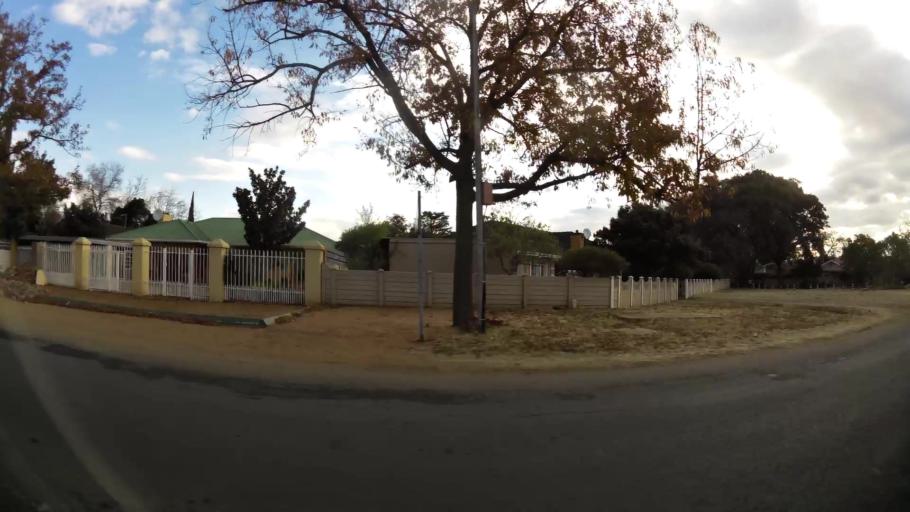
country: ZA
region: Orange Free State
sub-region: Lejweleputswa District Municipality
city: Welkom
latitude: -27.9964
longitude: 26.7333
